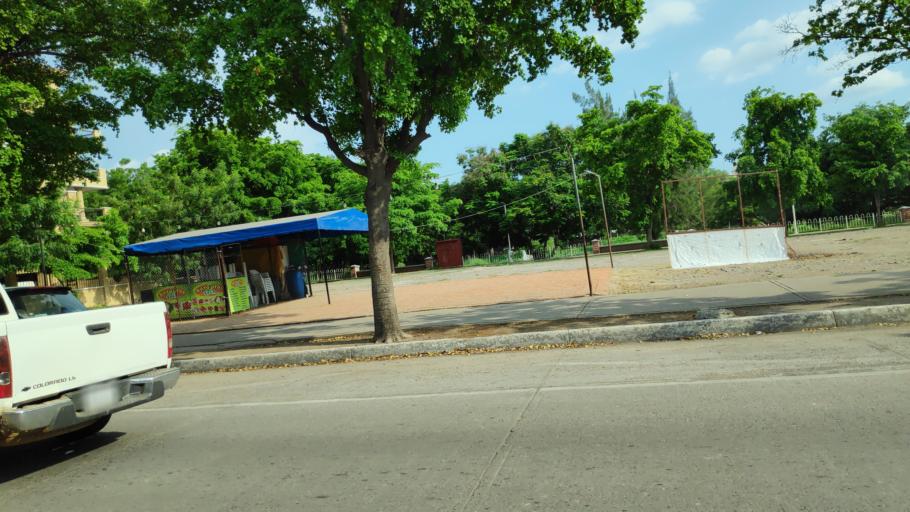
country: MX
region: Sinaloa
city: Culiacan
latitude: 24.8139
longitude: -107.3937
